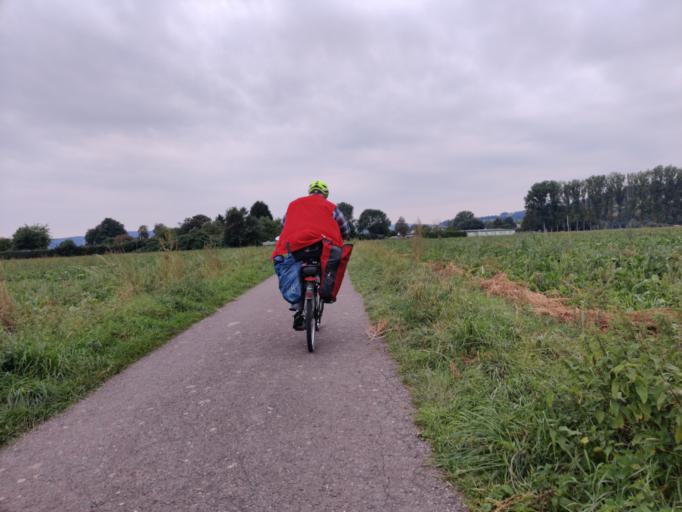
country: DE
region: Lower Saxony
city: Holzminden
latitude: 51.8395
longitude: 9.4409
